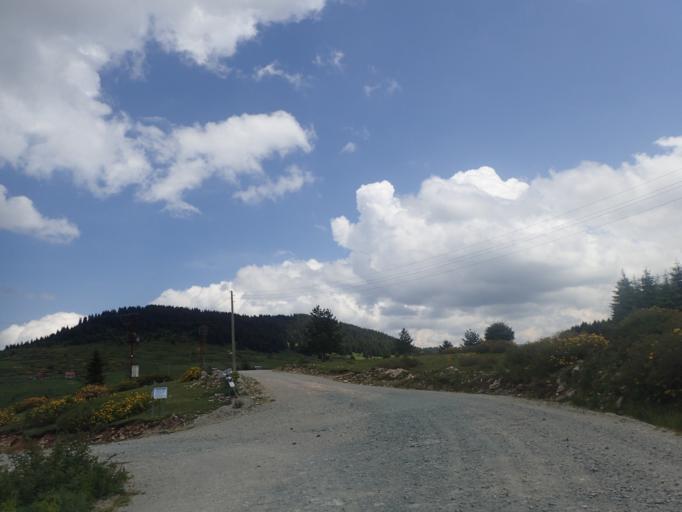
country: TR
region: Ordu
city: Topcam
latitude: 40.6820
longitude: 37.9400
